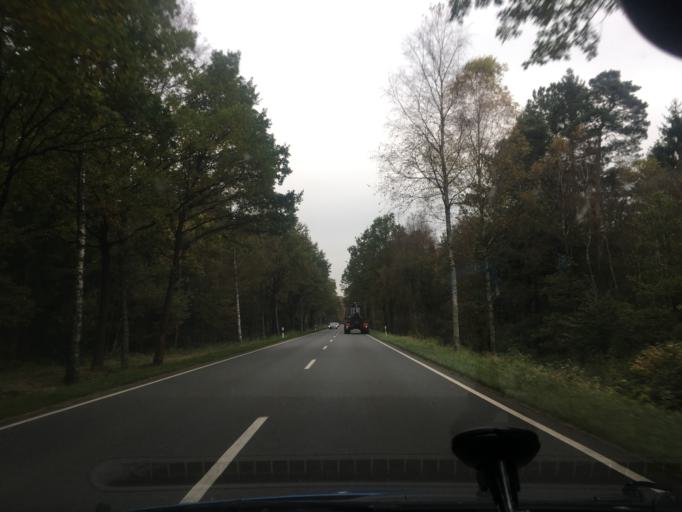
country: DE
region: Lower Saxony
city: Bispingen
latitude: 53.0513
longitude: 9.9927
